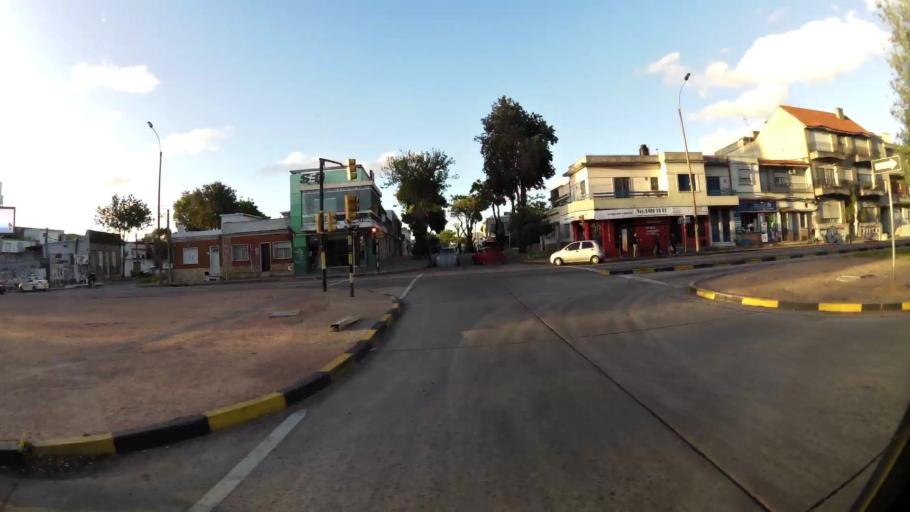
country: UY
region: Montevideo
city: Montevideo
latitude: -34.8872
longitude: -56.1419
